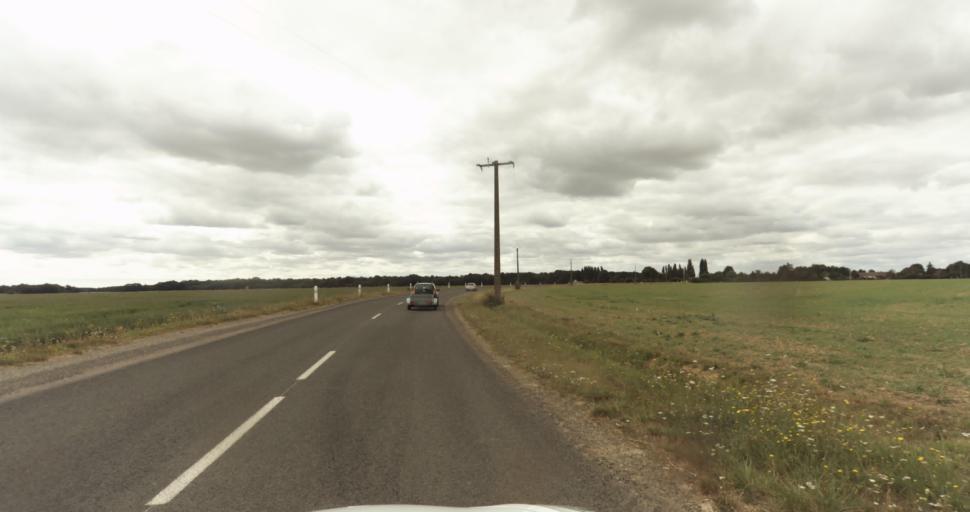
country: FR
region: Haute-Normandie
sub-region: Departement de l'Eure
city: La Madeleine-de-Nonancourt
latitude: 48.8348
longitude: 1.2296
